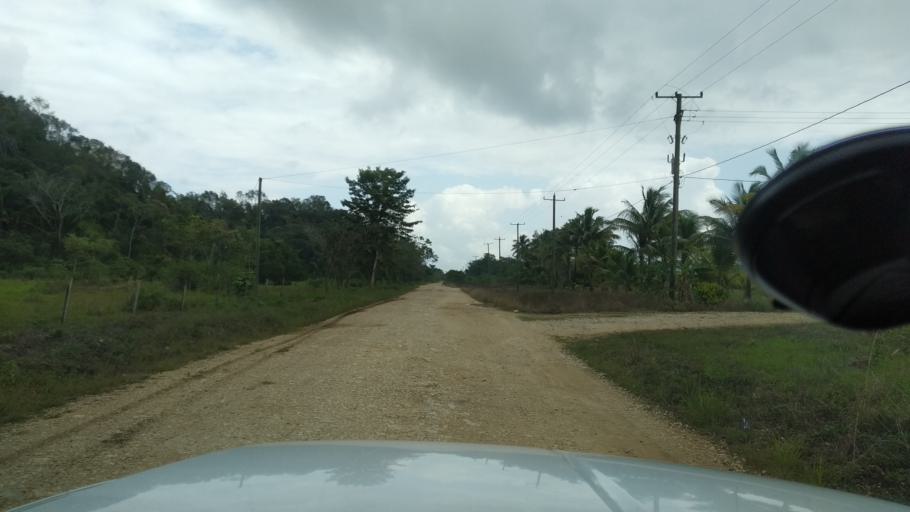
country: BZ
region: Toledo
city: Punta Gorda
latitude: 16.2161
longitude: -89.0069
